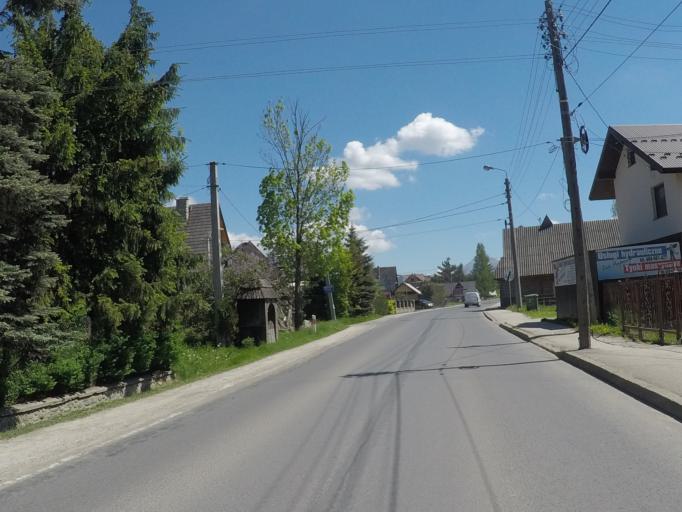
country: PL
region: Lesser Poland Voivodeship
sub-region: Powiat tatrzanski
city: Poronin
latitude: 49.3347
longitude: 20.0080
